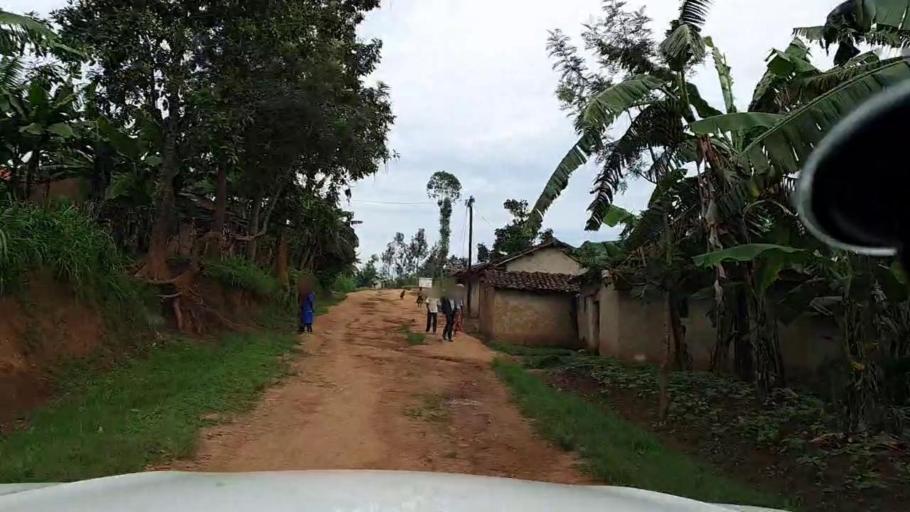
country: RW
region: Southern Province
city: Gitarama
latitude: -2.1159
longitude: 29.6393
